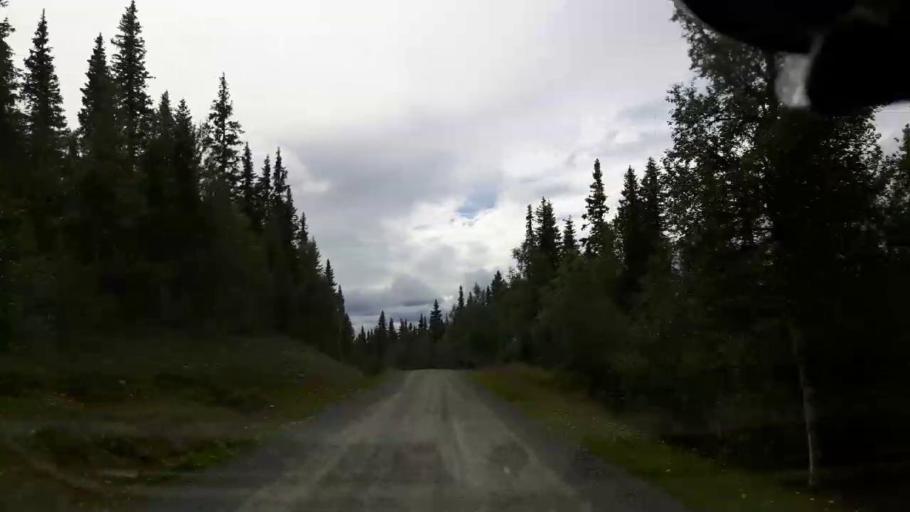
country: SE
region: Jaemtland
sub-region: Krokoms Kommun
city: Valla
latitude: 63.7542
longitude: 13.8365
